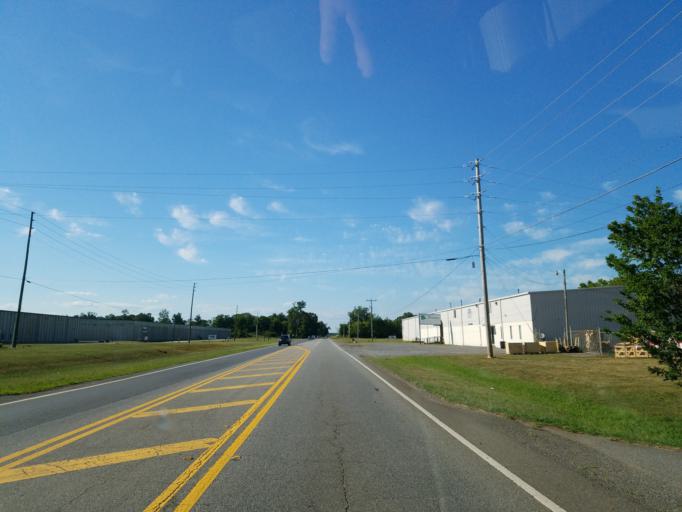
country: US
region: Georgia
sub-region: Bartow County
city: Adairsville
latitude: 34.4356
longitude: -84.9351
